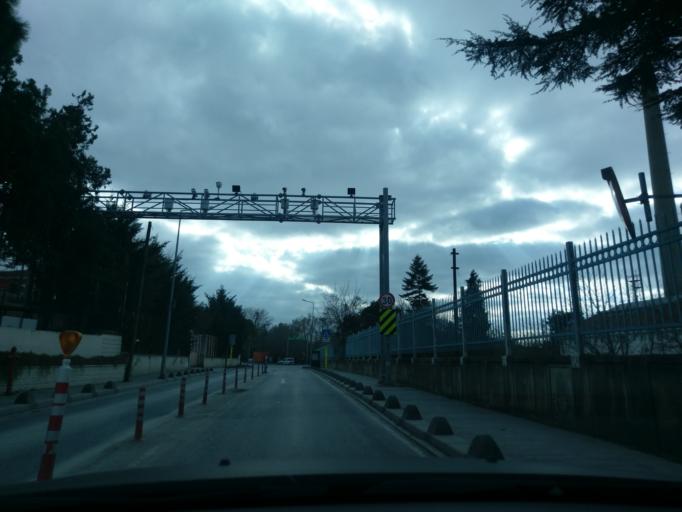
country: TR
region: Istanbul
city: Durusu
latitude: 41.3013
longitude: 28.6740
